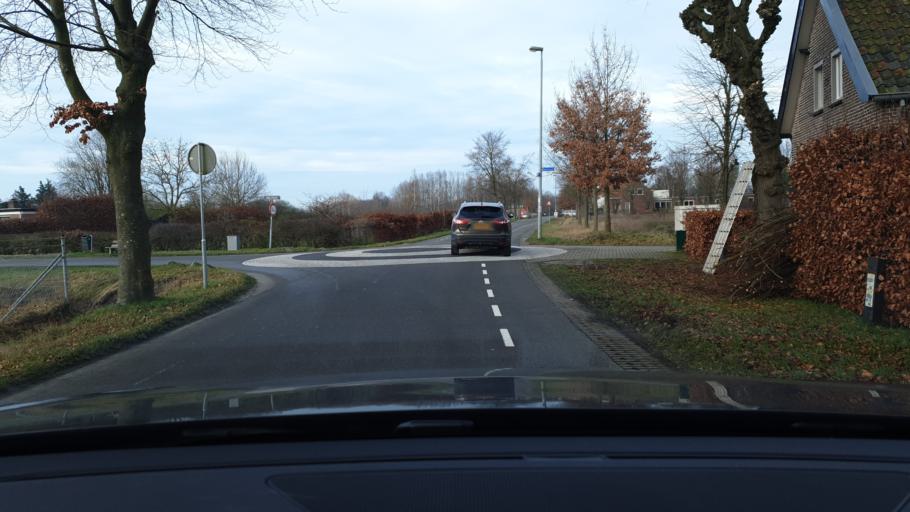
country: NL
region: North Brabant
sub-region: Gemeente Eindhoven
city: Muschberg en Geestenberg
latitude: 51.4363
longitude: 5.5334
